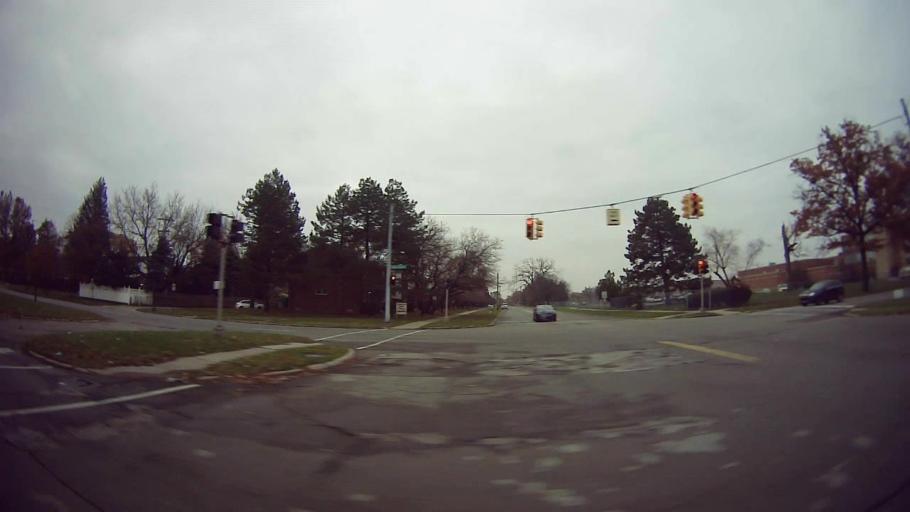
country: US
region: Michigan
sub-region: Oakland County
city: Oak Park
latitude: 42.4202
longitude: -83.1896
